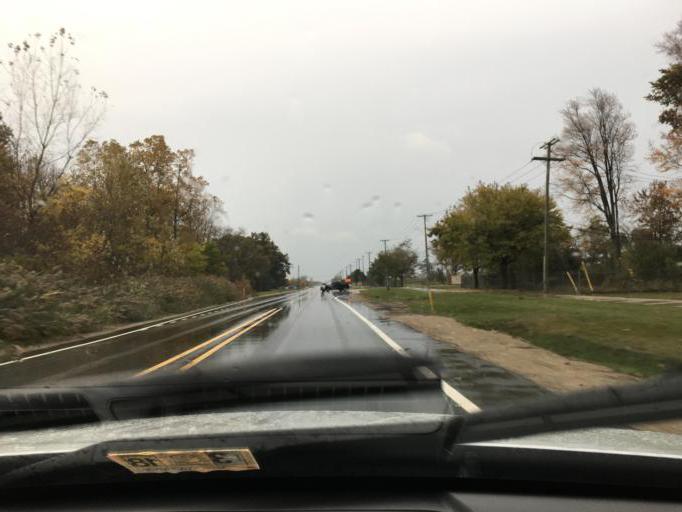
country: US
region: Michigan
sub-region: Oakland County
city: Troy
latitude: 42.6238
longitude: -83.1055
